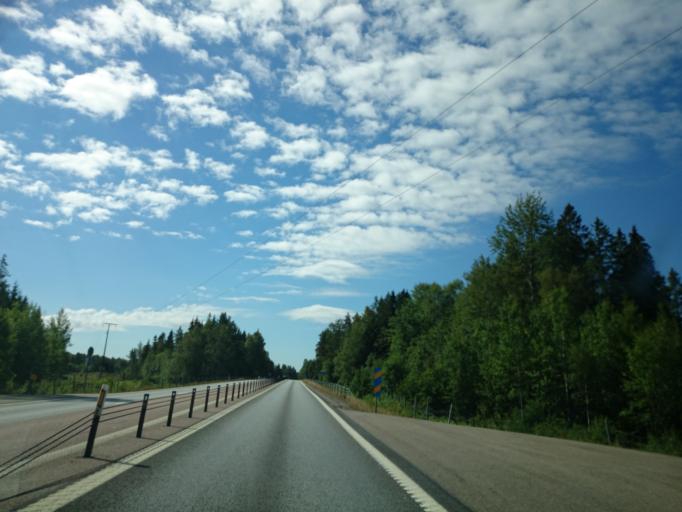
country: SE
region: Gaevleborg
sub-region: Soderhamns Kommun
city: Soderhamn
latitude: 61.2461
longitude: 17.0332
